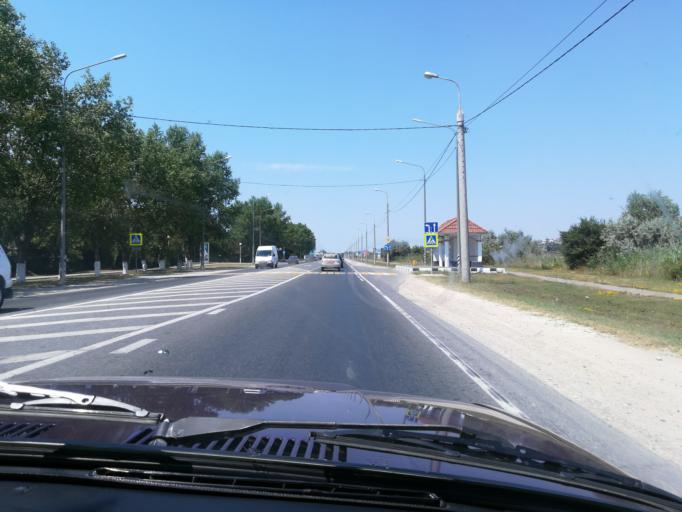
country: RU
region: Krasnodarskiy
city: Anapa
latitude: 44.9324
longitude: 37.3219
